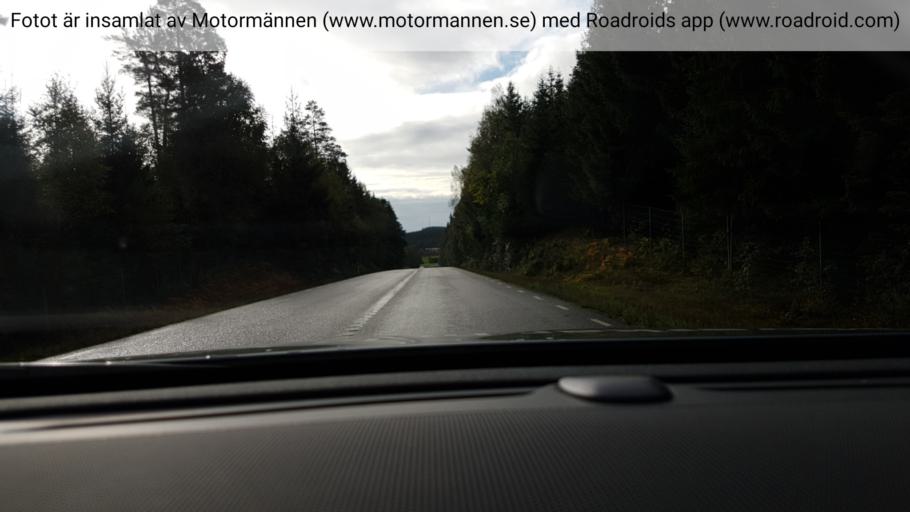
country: SE
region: Vaestra Goetaland
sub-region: Harryda Kommun
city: Ravlanda
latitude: 57.5613
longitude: 12.5157
